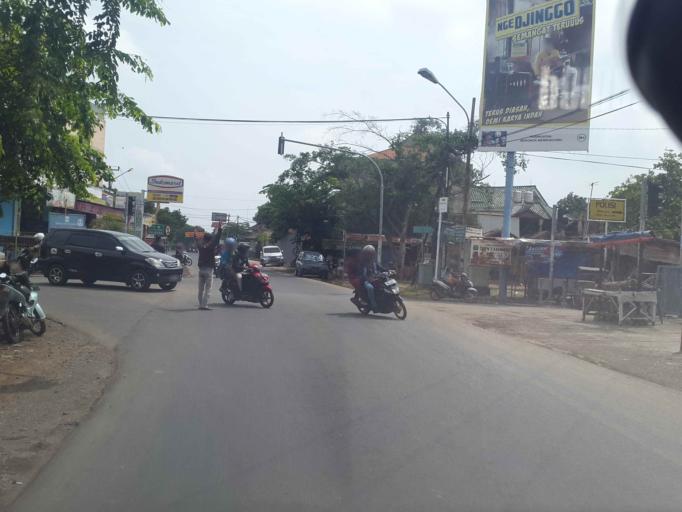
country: ID
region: West Java
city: Rengasdengklok
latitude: -6.2920
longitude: 107.3648
